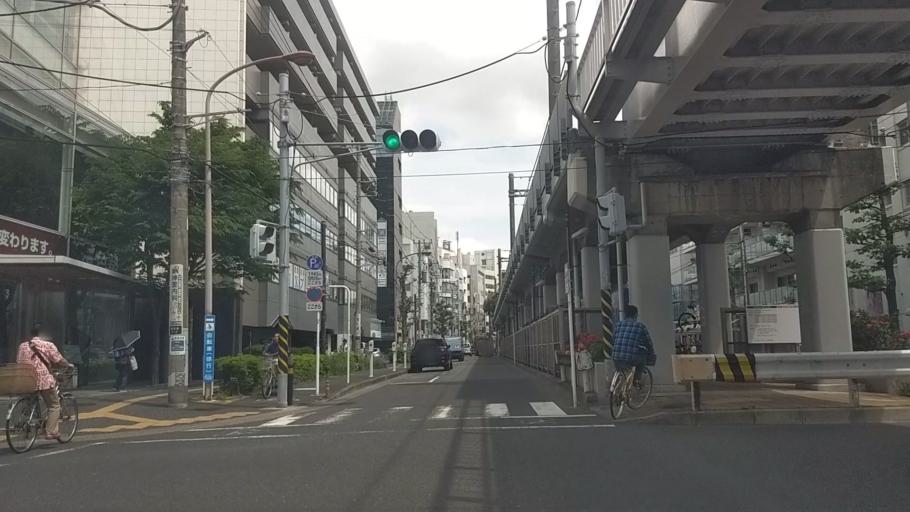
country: JP
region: Kanagawa
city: Fujisawa
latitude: 35.3348
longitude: 139.4861
